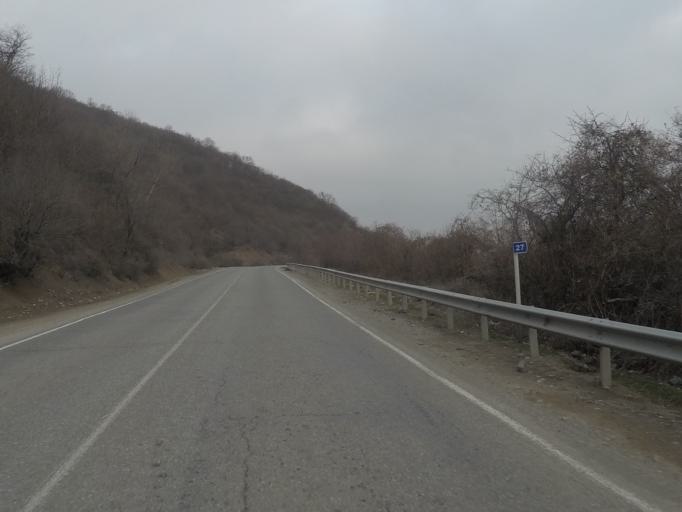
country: GE
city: Zhinvali
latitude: 42.1263
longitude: 44.7751
